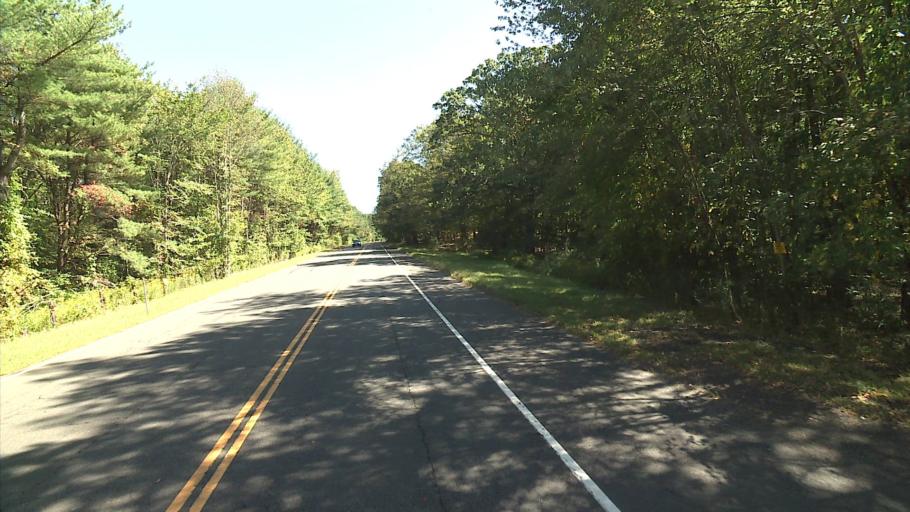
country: US
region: Connecticut
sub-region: New Haven County
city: Cheshire Village
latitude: 41.4980
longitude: -72.8621
